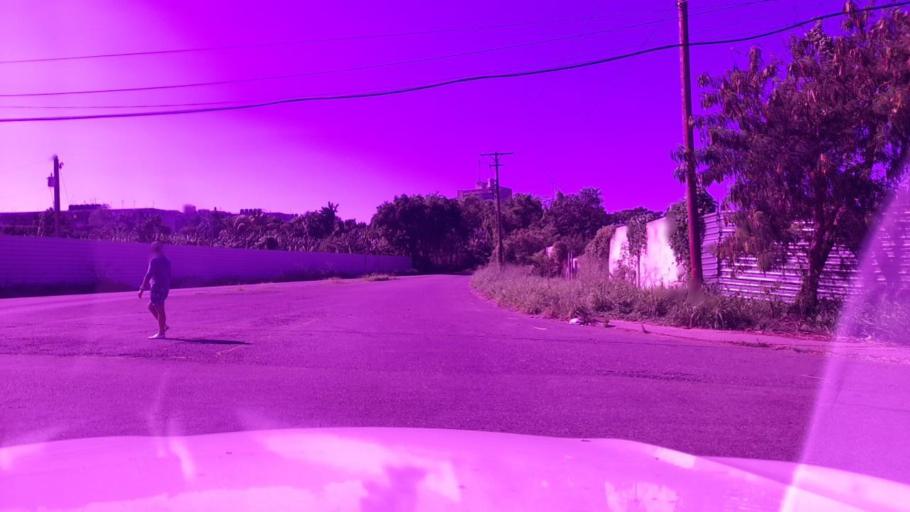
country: CU
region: La Habana
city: Alamar
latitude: 23.1656
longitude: -82.2735
